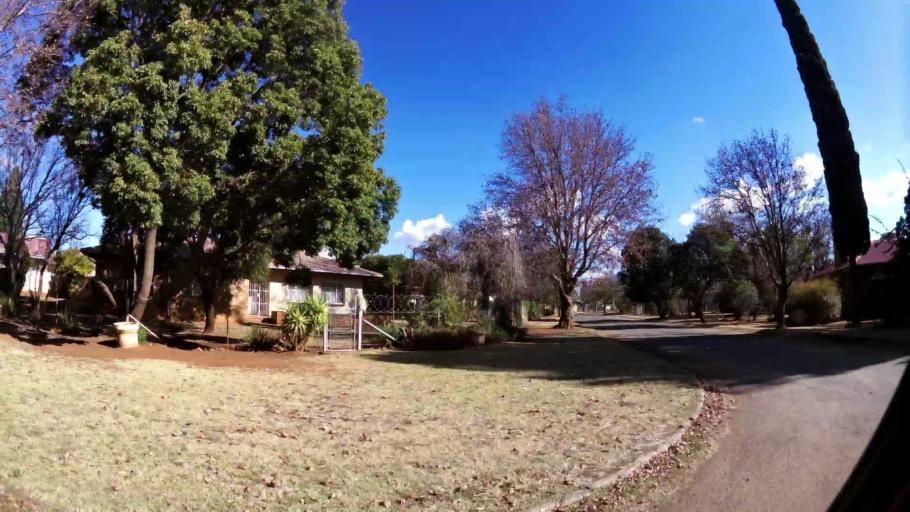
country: ZA
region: Gauteng
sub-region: West Rand District Municipality
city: Carletonville
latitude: -26.3609
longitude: 27.3652
